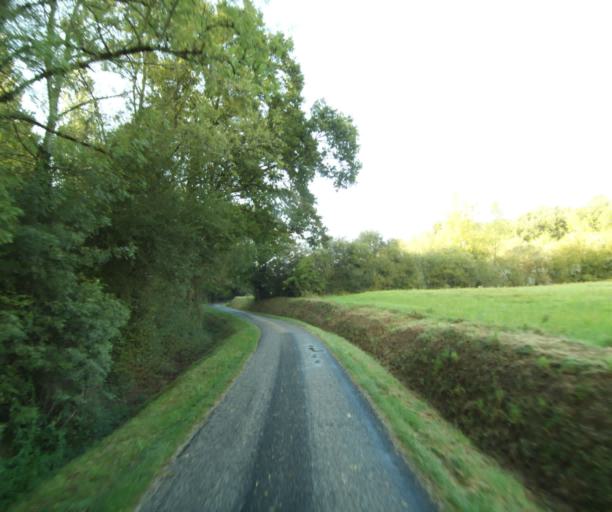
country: FR
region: Midi-Pyrenees
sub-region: Departement du Gers
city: Cazaubon
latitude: 43.9173
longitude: -0.0506
